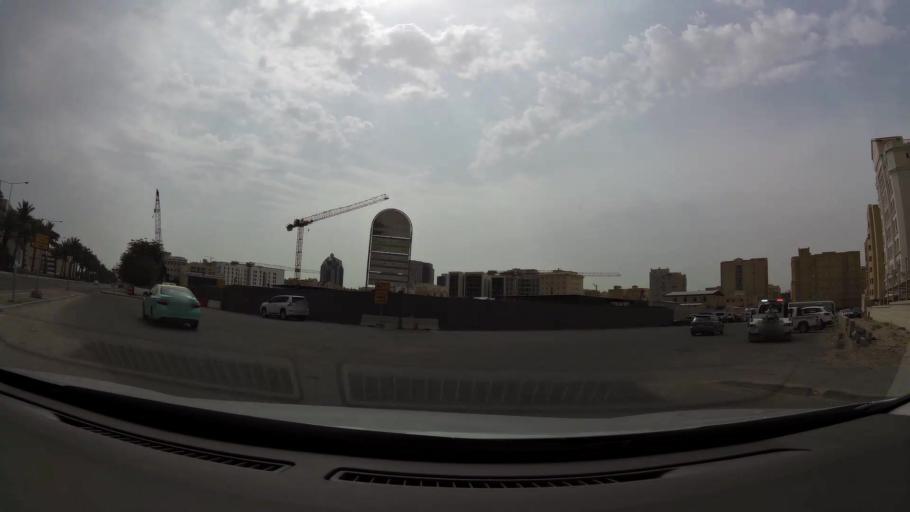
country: QA
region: Baladiyat ad Dawhah
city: Doha
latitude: 25.2917
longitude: 51.4989
